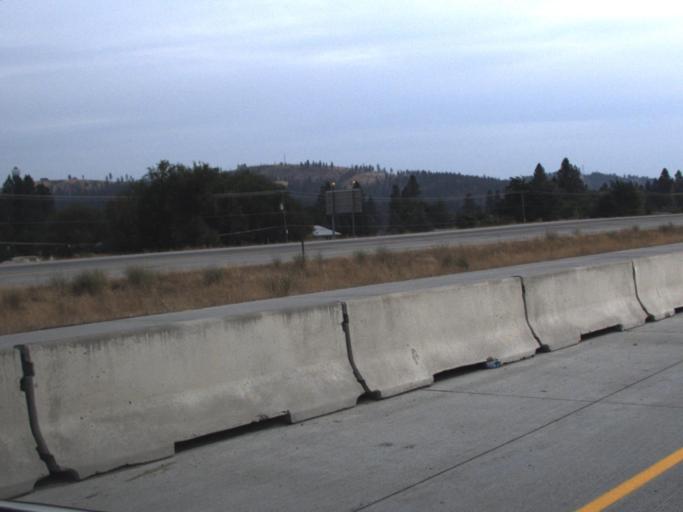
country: US
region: Washington
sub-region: Franklin County
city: Pasco
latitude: 46.2650
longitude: -119.0837
